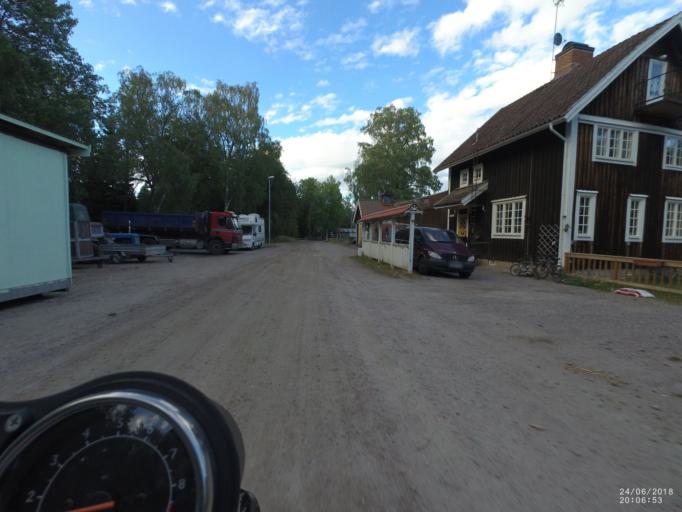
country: SE
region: Soedermanland
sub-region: Nykopings Kommun
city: Nykoping
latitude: 58.8134
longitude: 17.1430
